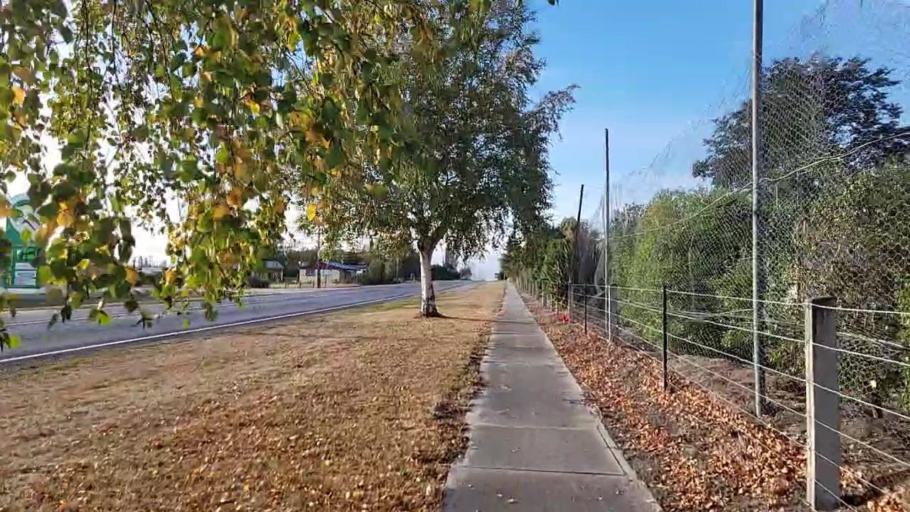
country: NZ
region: Southland
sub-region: Gore District
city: Gore
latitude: -45.6392
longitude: 169.3702
